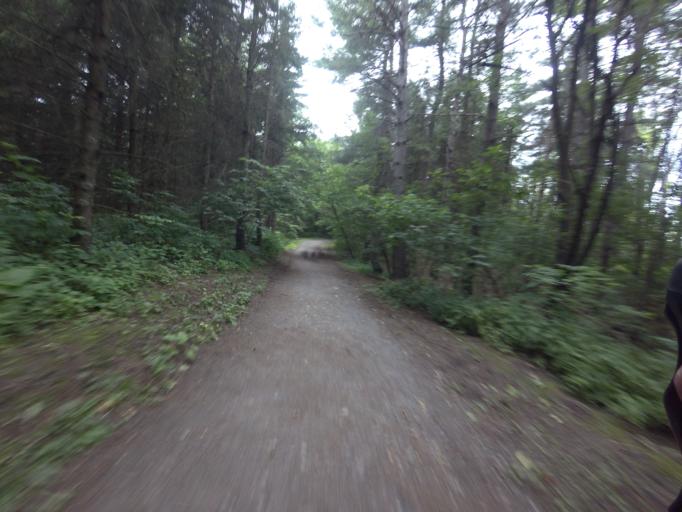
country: CA
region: Ontario
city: Bells Corners
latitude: 45.2571
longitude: -75.7064
